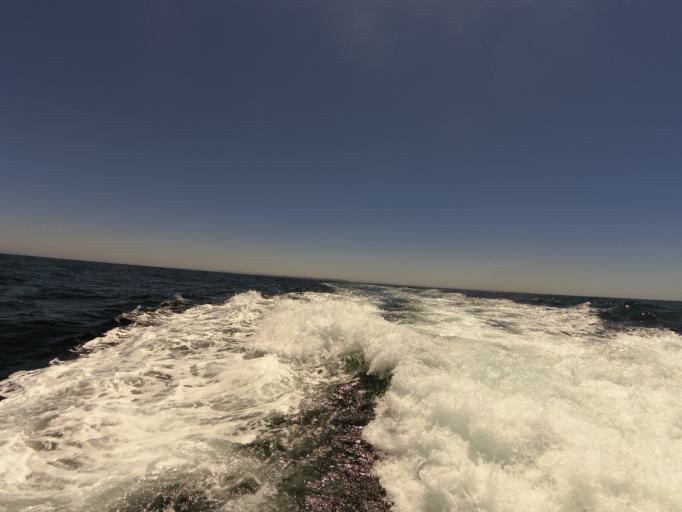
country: PT
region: Leiria
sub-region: Peniche
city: Peniche
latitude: 39.3895
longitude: -9.4713
